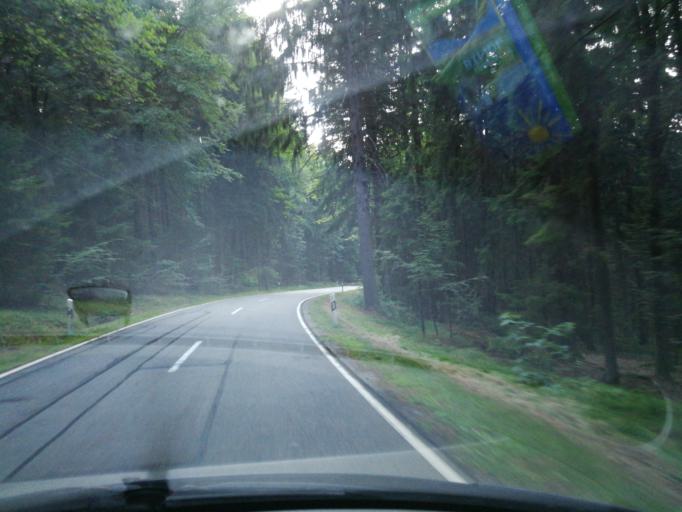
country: DE
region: Bavaria
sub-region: Lower Bavaria
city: Haibach
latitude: 49.0246
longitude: 12.7397
